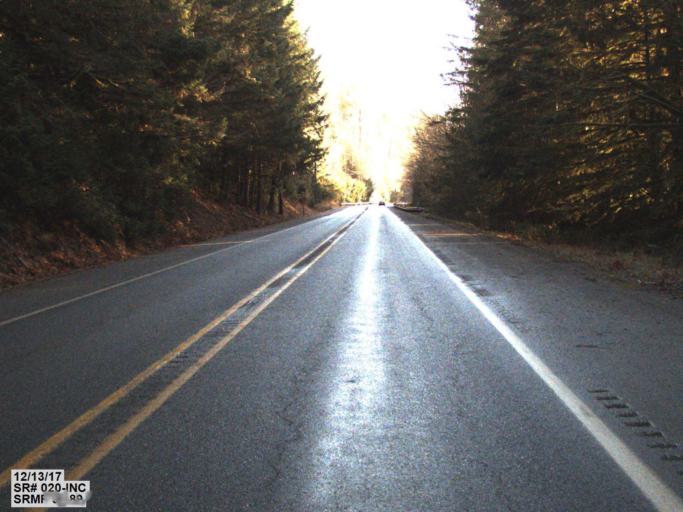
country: US
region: Washington
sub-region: Snohomish County
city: Darrington
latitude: 48.4875
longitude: -121.6069
